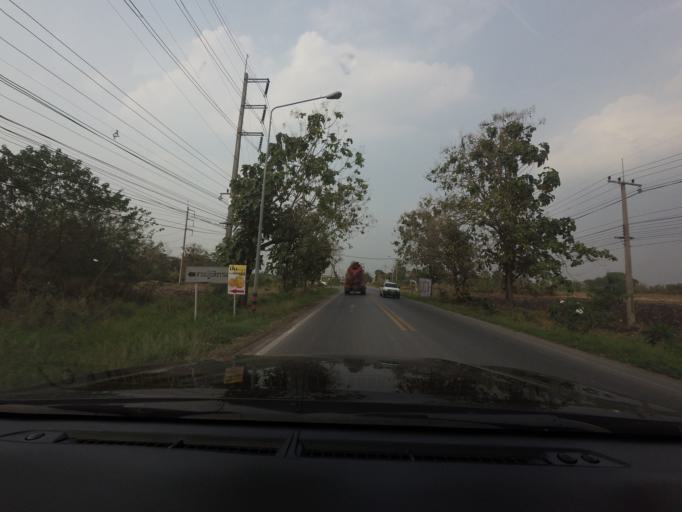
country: TH
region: Sara Buri
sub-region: Amphoe Wang Muang
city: Wang Muang
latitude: 14.8331
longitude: 101.1227
